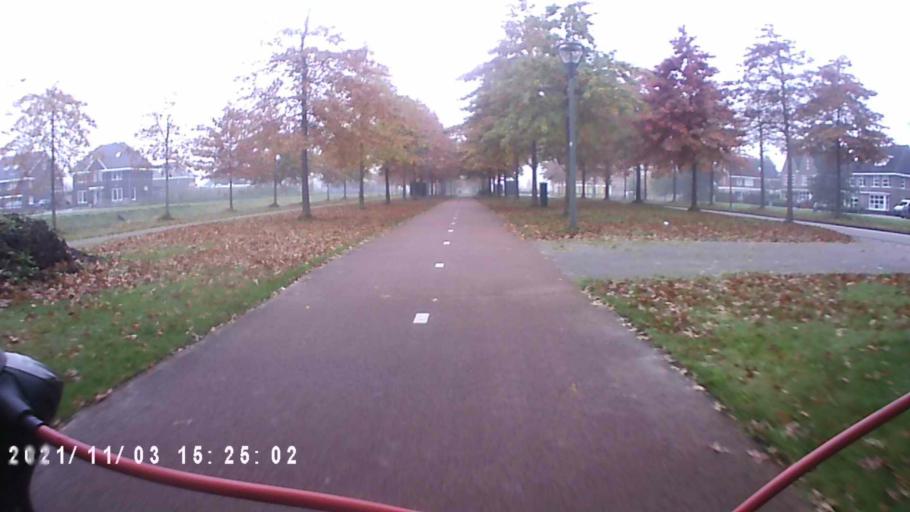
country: NL
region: Groningen
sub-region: Gemeente Leek
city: Leek
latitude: 53.1483
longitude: 6.3731
